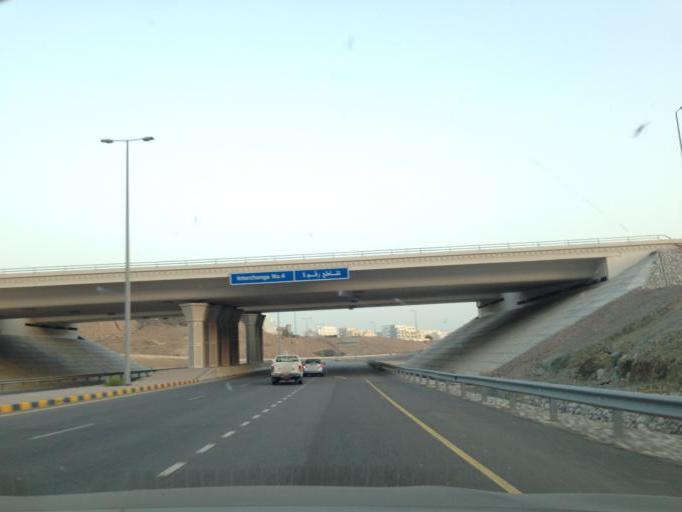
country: OM
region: Muhafazat Masqat
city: Bawshar
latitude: 23.5814
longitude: 58.4453
